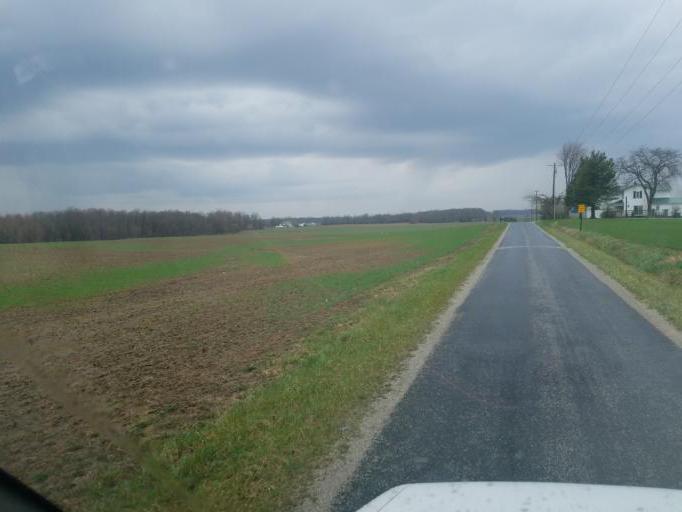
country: US
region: Ohio
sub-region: Crawford County
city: Galion
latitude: 40.6838
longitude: -82.8515
